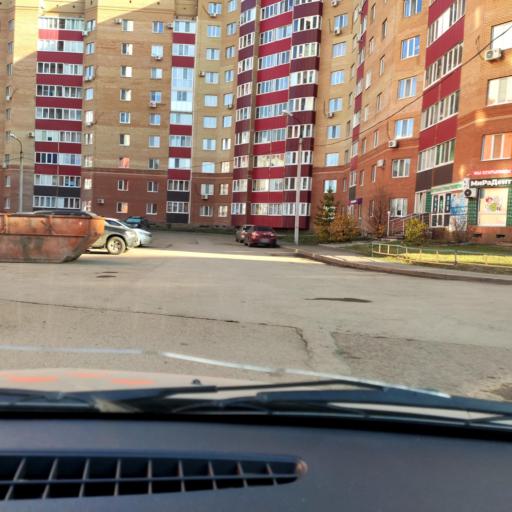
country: RU
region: Bashkortostan
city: Mikhaylovka
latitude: 54.7137
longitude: 55.8368
